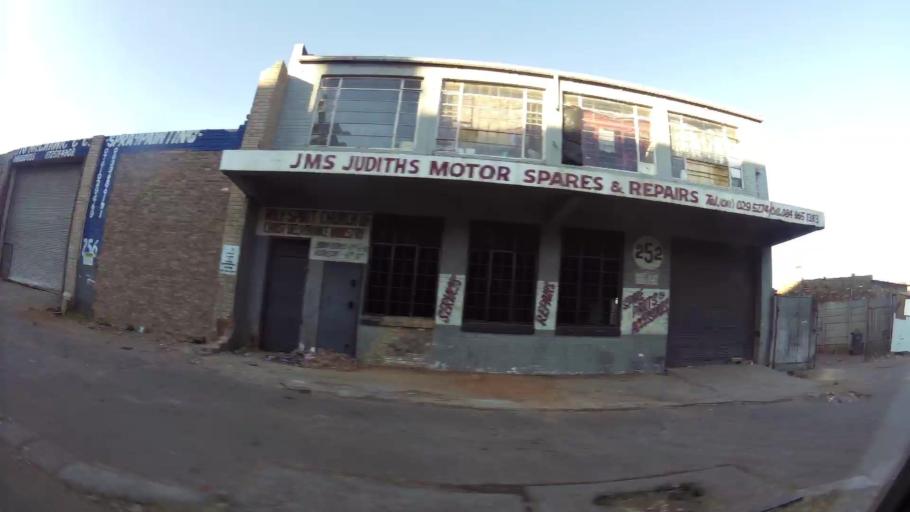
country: ZA
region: Gauteng
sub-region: City of Johannesburg Metropolitan Municipality
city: Johannesburg
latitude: -26.2070
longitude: 28.0897
